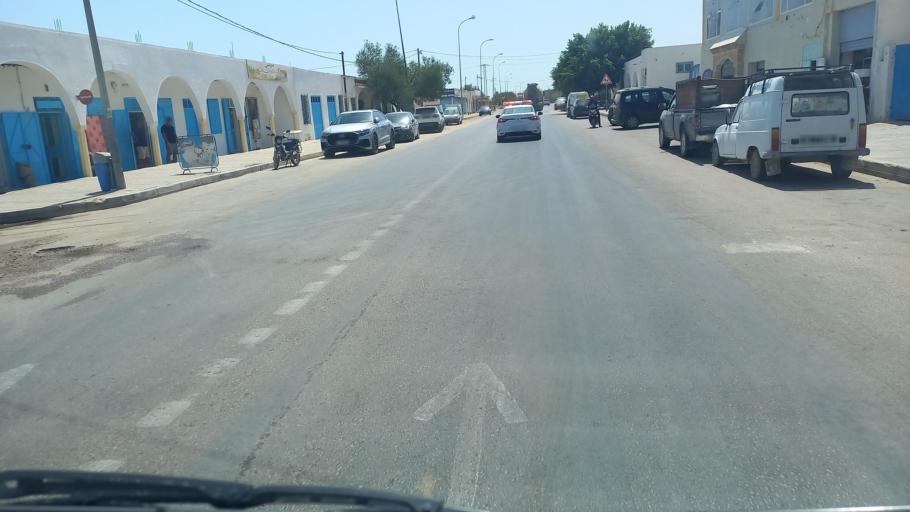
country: TN
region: Madanin
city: Midoun
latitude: 33.7756
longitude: 10.8947
